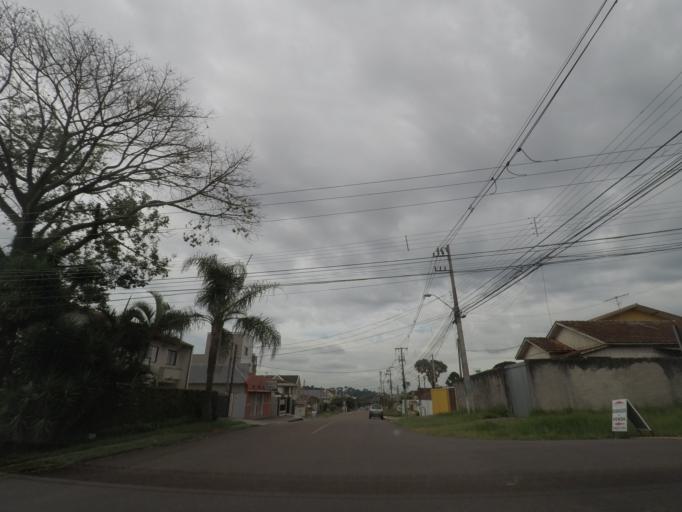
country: BR
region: Parana
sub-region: Pinhais
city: Pinhais
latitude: -25.4699
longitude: -49.2293
